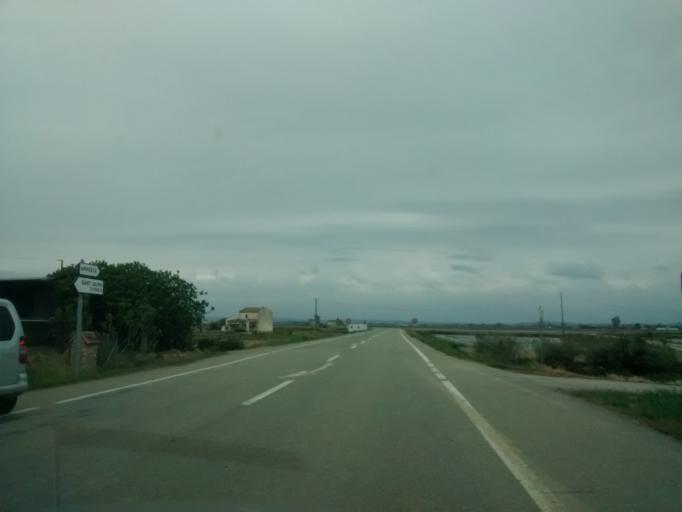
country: ES
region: Catalonia
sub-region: Provincia de Tarragona
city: Deltebre
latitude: 40.7013
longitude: 0.6742
